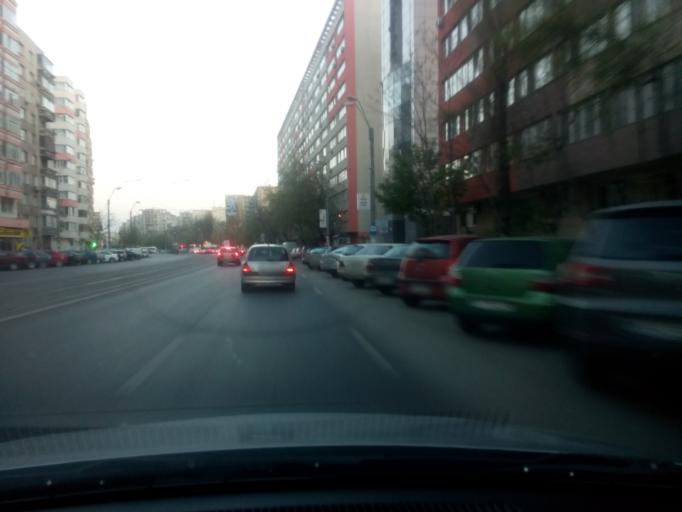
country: RO
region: Bucuresti
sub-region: Municipiul Bucuresti
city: Bucharest
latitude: 44.4456
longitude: 26.1270
